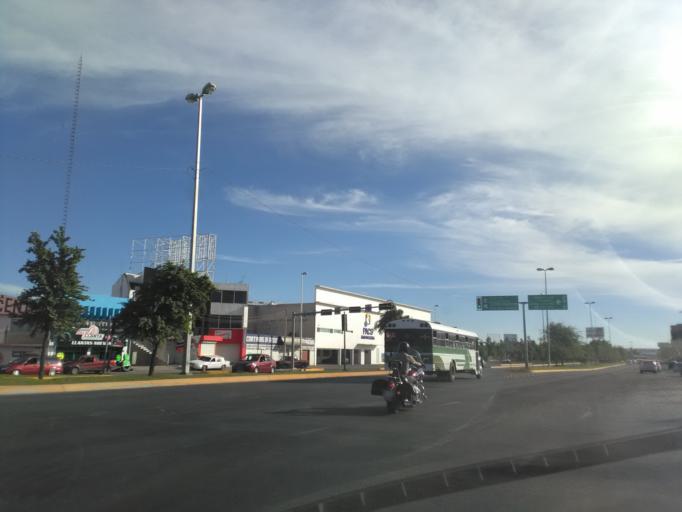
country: MX
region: Durango
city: Victoria de Durango
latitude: 24.0349
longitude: -104.6372
